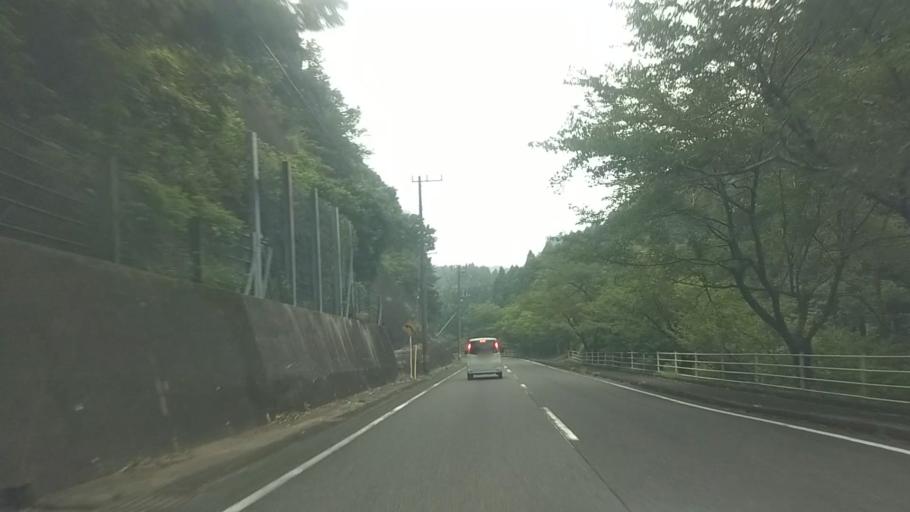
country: JP
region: Chiba
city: Kawaguchi
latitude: 35.2368
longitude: 140.1638
